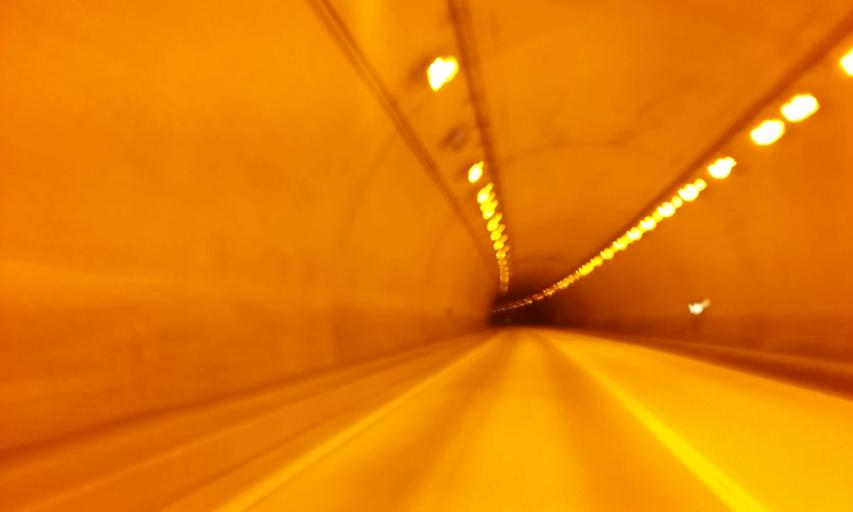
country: JP
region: Kyoto
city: Kameoka
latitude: 35.2215
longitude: 135.5718
